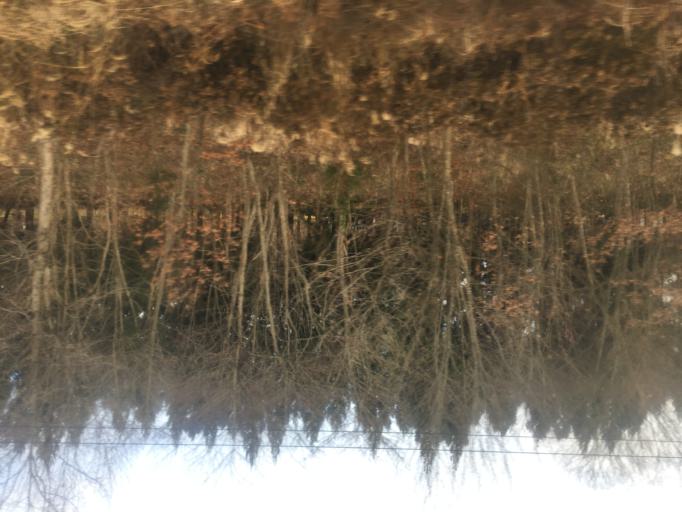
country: JP
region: Akita
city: Takanosu
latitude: 40.2389
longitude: 140.3837
